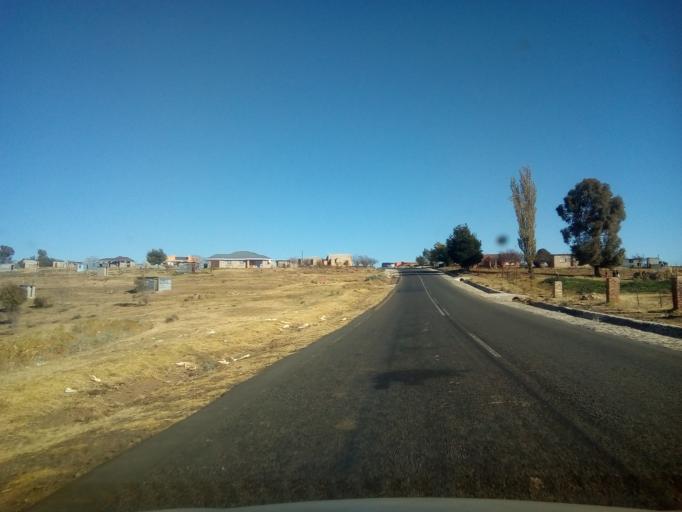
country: LS
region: Maseru
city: Maseru
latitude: -29.2930
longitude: 27.6214
